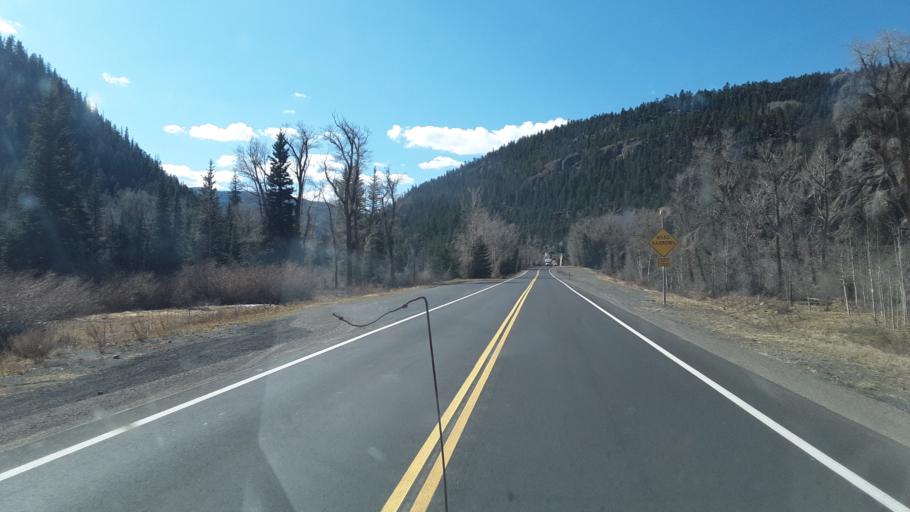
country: US
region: Colorado
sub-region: Mineral County
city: Creede
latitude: 37.6073
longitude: -106.7218
